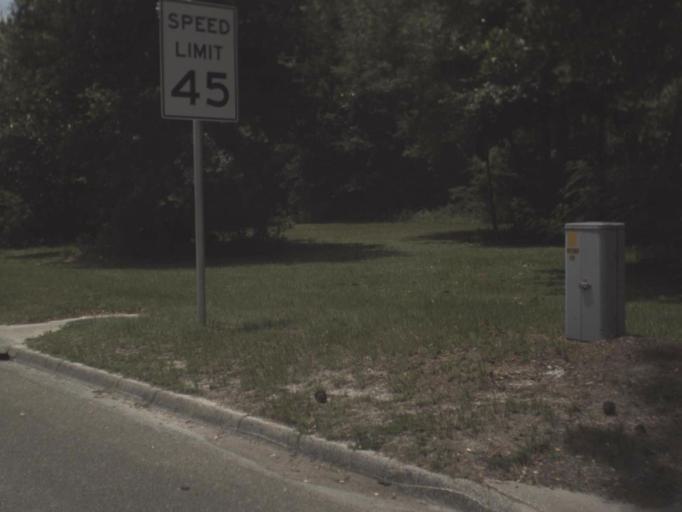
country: US
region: Florida
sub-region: Taylor County
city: Perry
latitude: 30.0842
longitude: -83.5690
